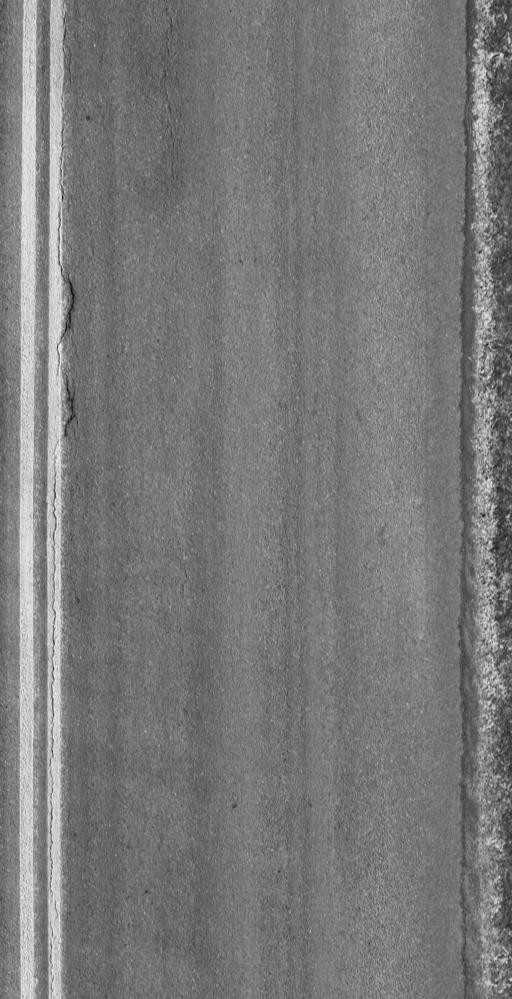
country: US
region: Vermont
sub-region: Chittenden County
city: Hinesburg
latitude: 44.3270
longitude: -73.1908
